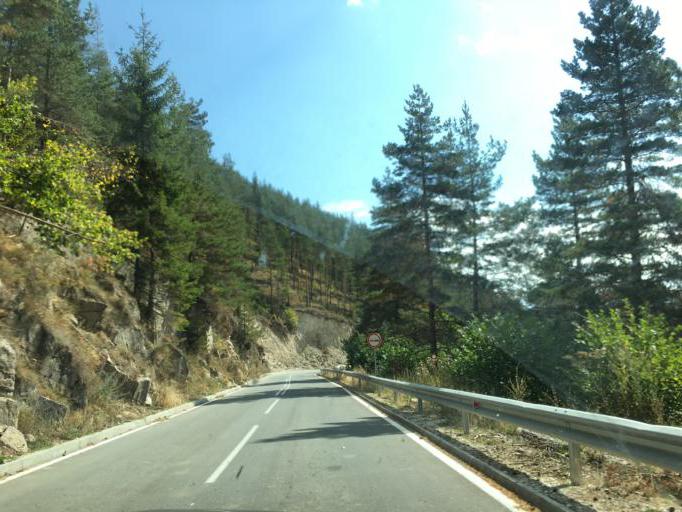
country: BG
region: Pazardzhik
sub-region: Obshtina Bratsigovo
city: Bratsigovo
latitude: 41.8879
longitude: 24.3350
